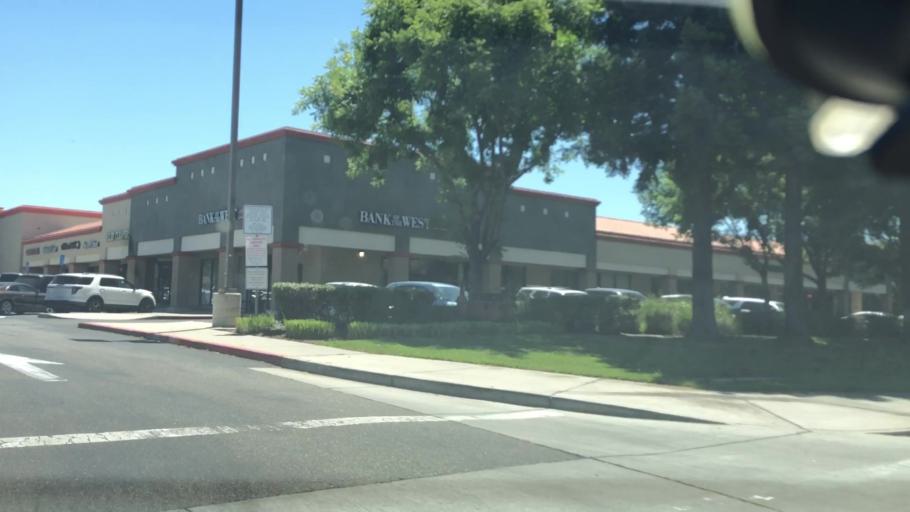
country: US
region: California
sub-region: San Joaquin County
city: Tracy
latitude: 37.7250
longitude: -121.4366
